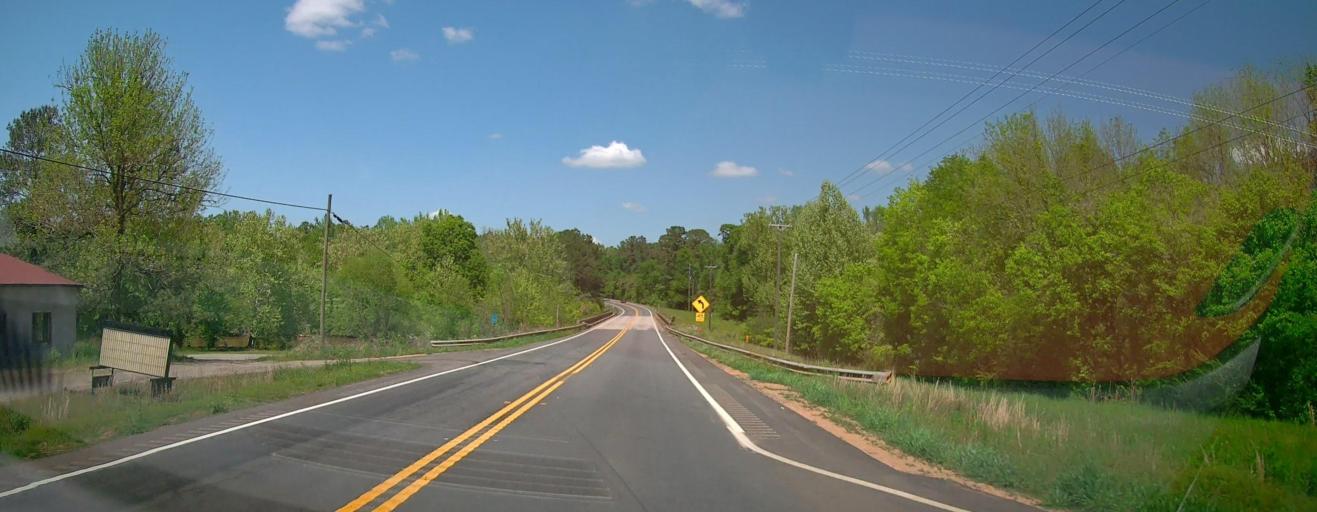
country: US
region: Georgia
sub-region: Putnam County
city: Eatonton
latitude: 33.2170
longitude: -83.4310
